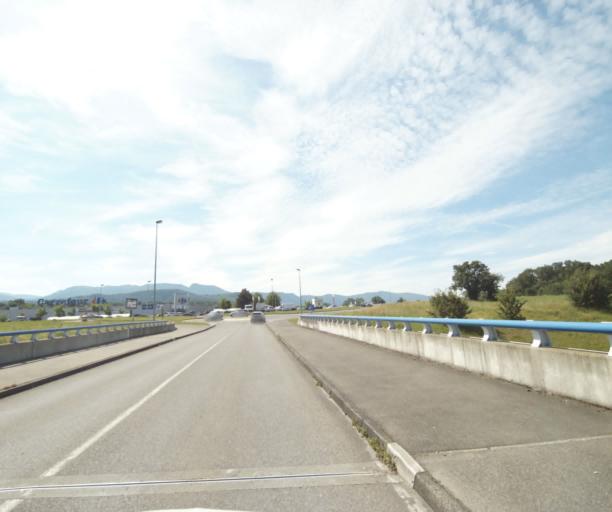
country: FR
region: Rhone-Alpes
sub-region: Departement de la Haute-Savoie
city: Anthy-sur-Leman
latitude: 46.3471
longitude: 6.4329
